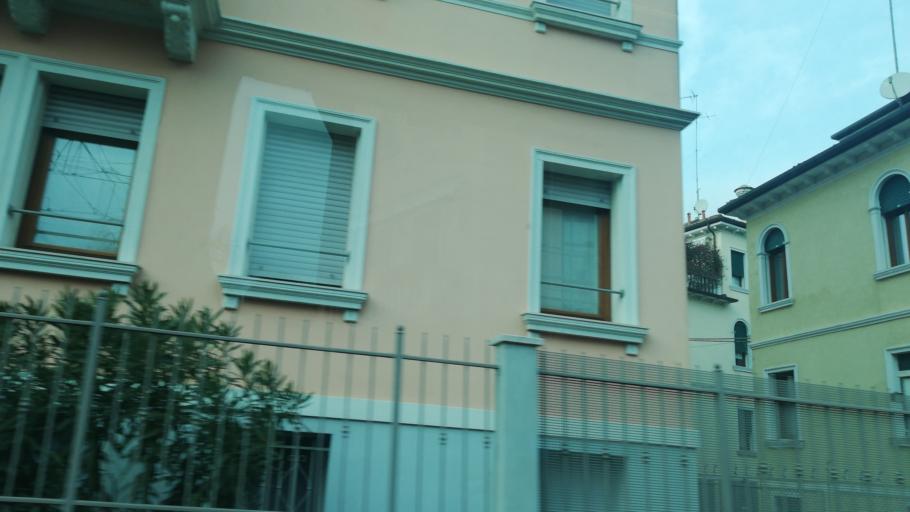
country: IT
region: Veneto
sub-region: Provincia di Venezia
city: Mestre
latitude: 45.4941
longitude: 12.2468
